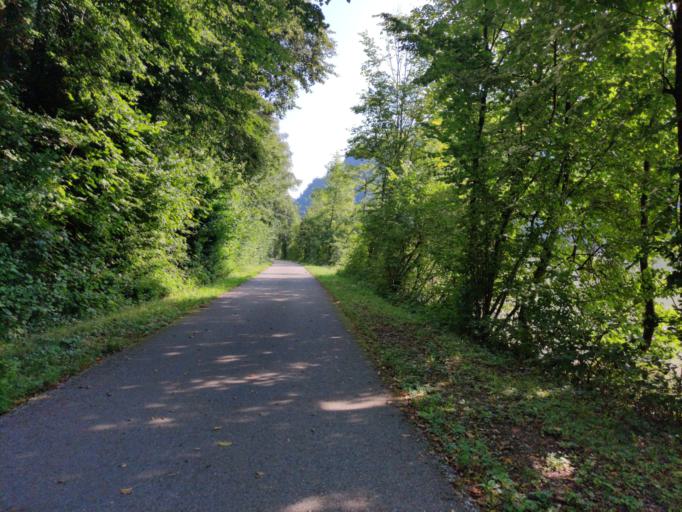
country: AT
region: Upper Austria
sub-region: Politischer Bezirk Rohrbach
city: Kleinzell im Muehlkreis
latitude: 48.4066
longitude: 13.9479
